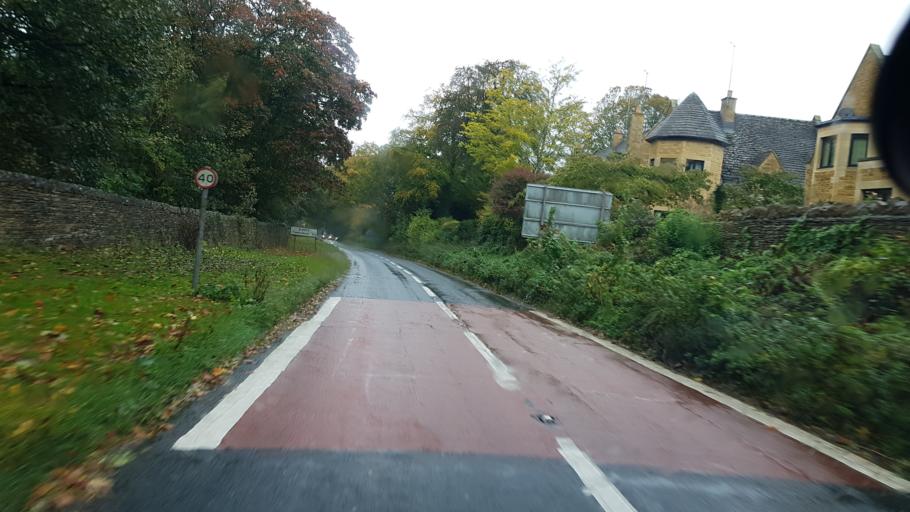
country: GB
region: England
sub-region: Gloucestershire
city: Stow on the Wold
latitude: 51.9336
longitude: -1.7262
